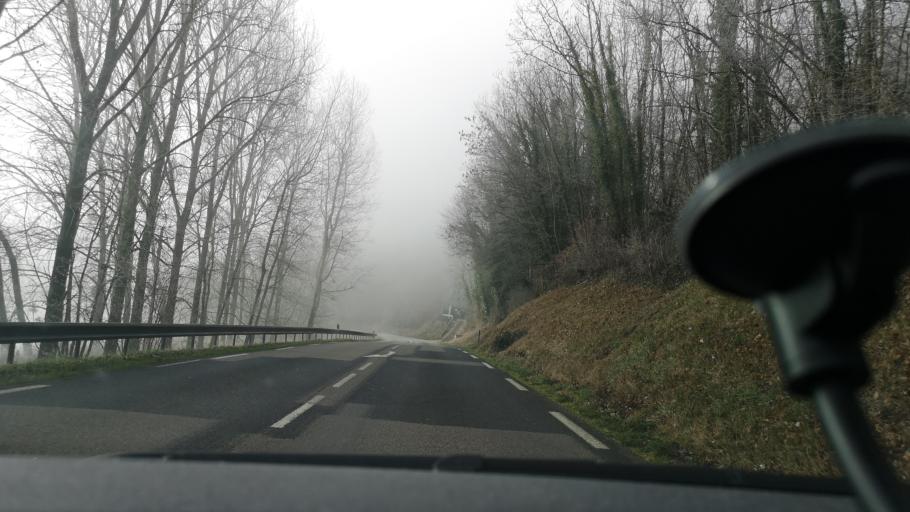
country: FR
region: Franche-Comte
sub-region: Departement du Doubs
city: Clerval
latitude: 47.3723
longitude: 6.4542
